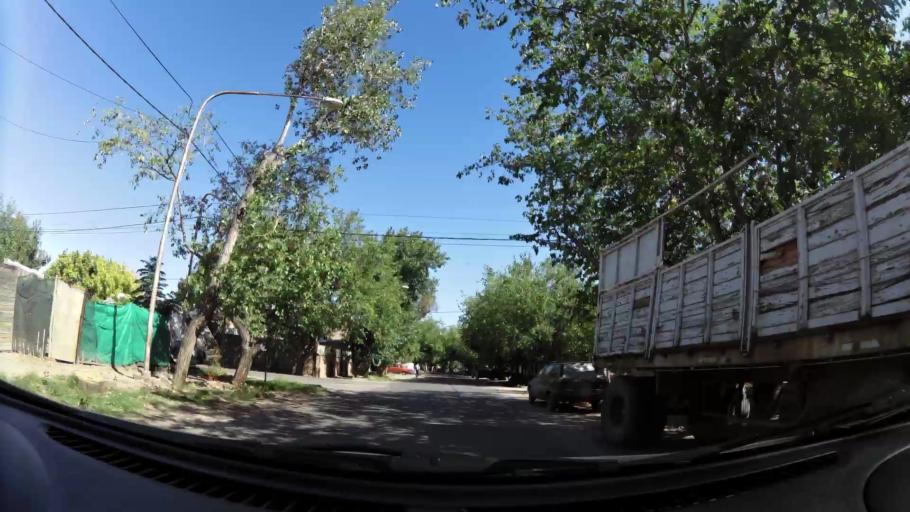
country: AR
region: Mendoza
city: Mendoza
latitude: -32.8819
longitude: -68.8116
